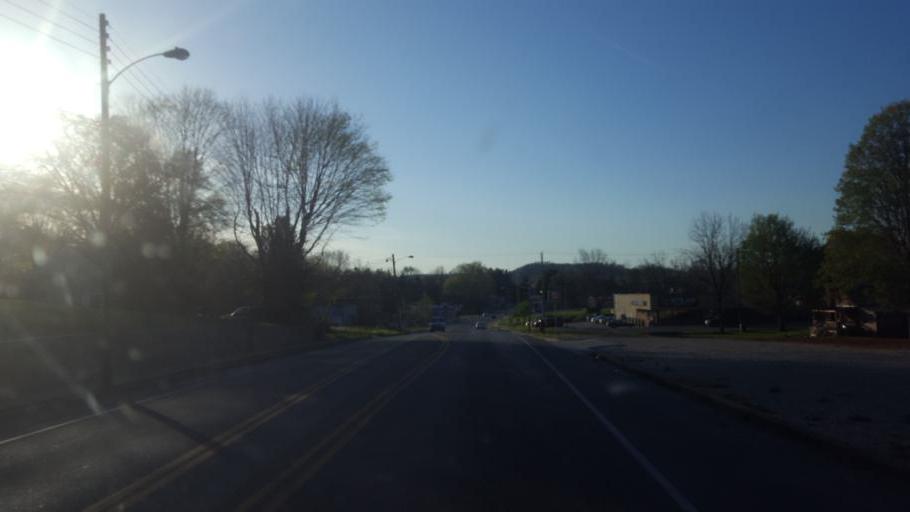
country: US
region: Kentucky
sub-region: Hart County
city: Munfordville
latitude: 37.2731
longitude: -85.8929
